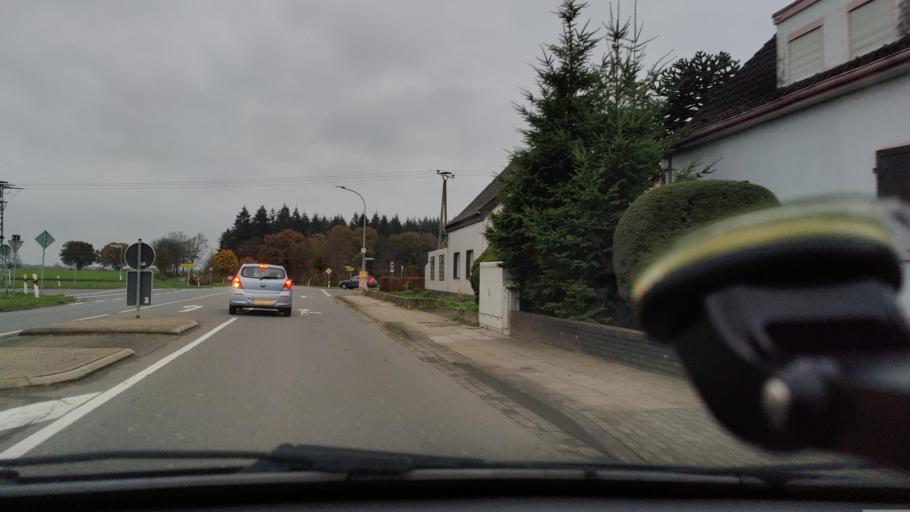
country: DE
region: North Rhine-Westphalia
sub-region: Regierungsbezirk Dusseldorf
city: Alpen
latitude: 51.5695
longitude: 6.5244
